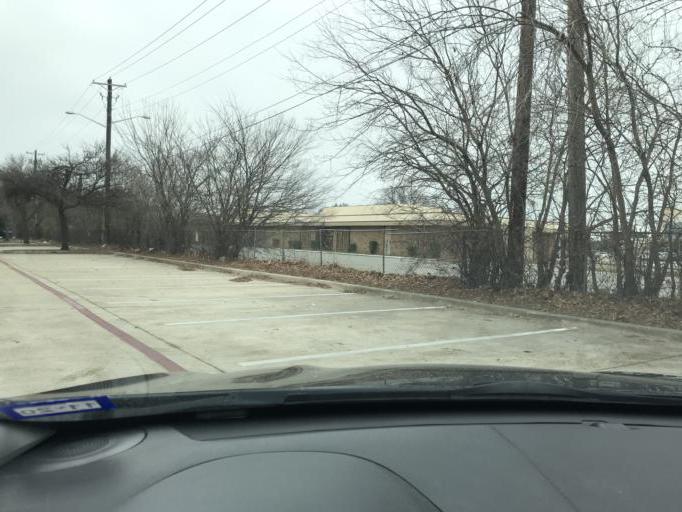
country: US
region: Texas
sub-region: Denton County
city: Denton
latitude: 33.2272
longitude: -97.1496
